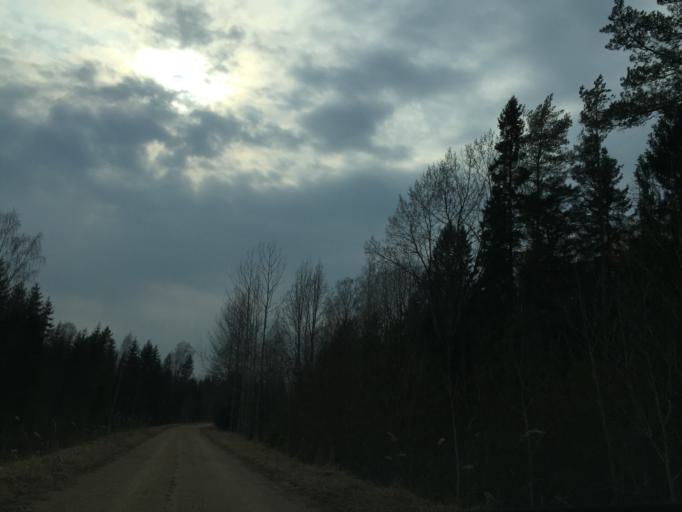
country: LV
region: Amatas Novads
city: Drabesi
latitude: 57.1985
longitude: 25.3749
